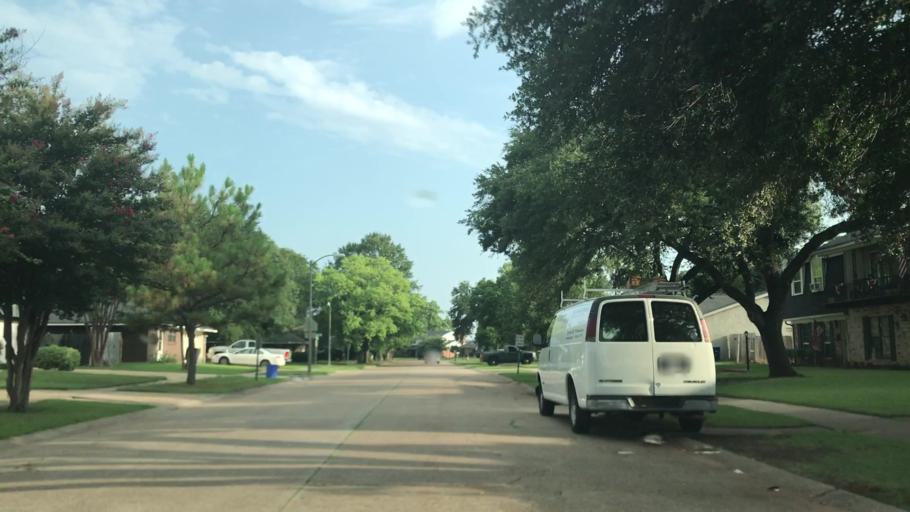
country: US
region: Louisiana
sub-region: Bossier Parish
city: Bossier City
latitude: 32.4153
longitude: -93.7033
